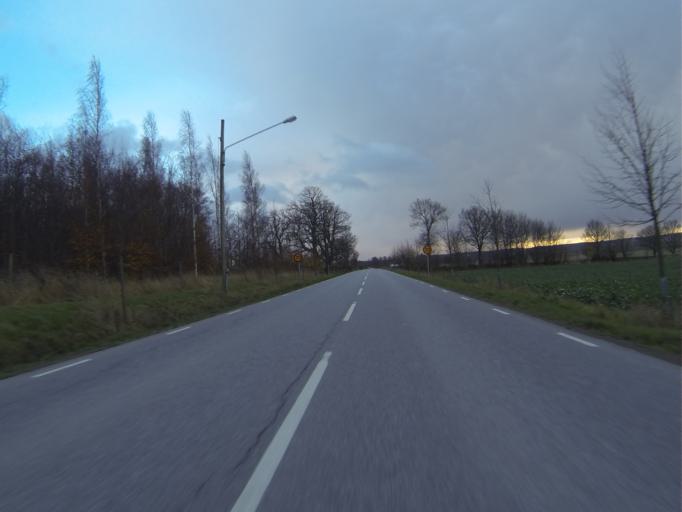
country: SE
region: Skane
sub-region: Lunds Kommun
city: Genarp
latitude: 55.6206
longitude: 13.4059
